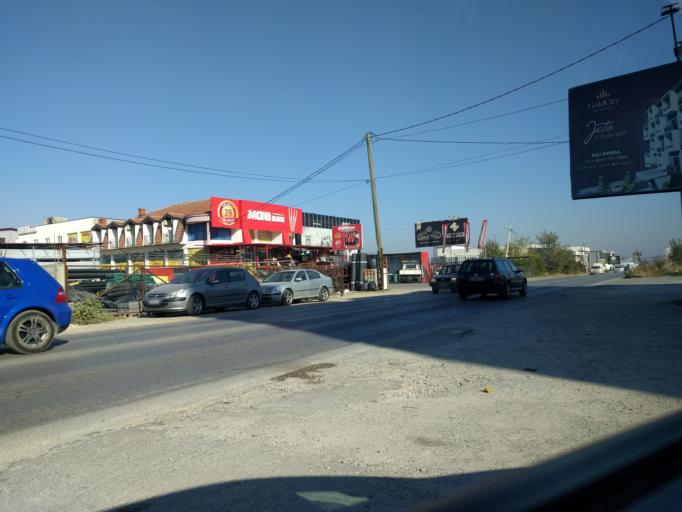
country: XK
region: Prizren
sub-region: Prizren
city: Prizren
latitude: 42.2388
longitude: 20.7622
